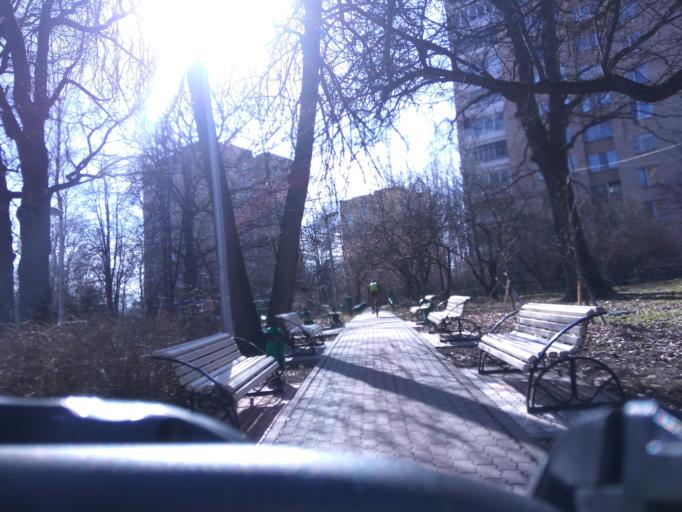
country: RU
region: Moscow
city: Davydkovo
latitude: 55.7345
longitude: 37.4502
